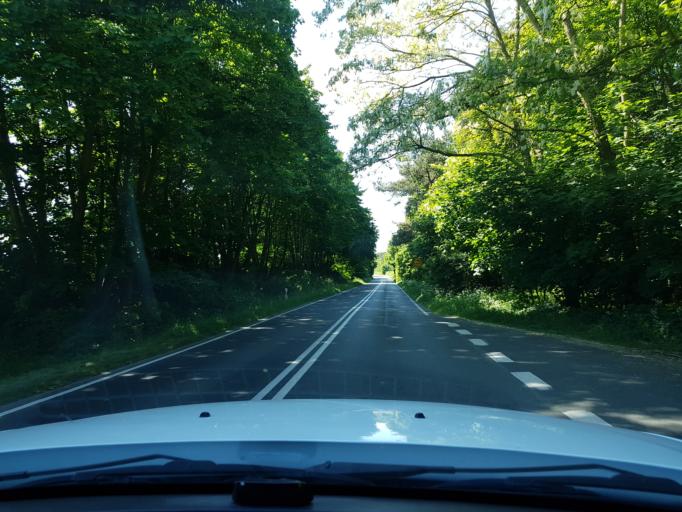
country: PL
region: West Pomeranian Voivodeship
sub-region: Powiat gryfinski
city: Gryfino
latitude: 53.1818
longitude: 14.5485
